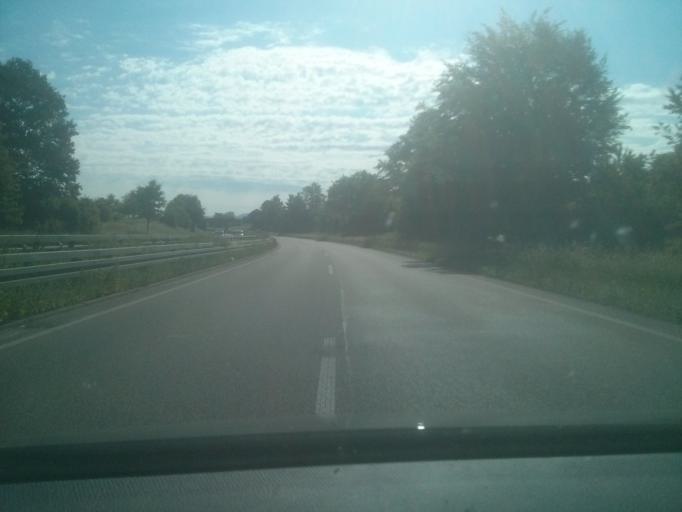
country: DE
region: Baden-Wuerttemberg
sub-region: Tuebingen Region
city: Wannweil
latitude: 48.4969
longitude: 9.1326
